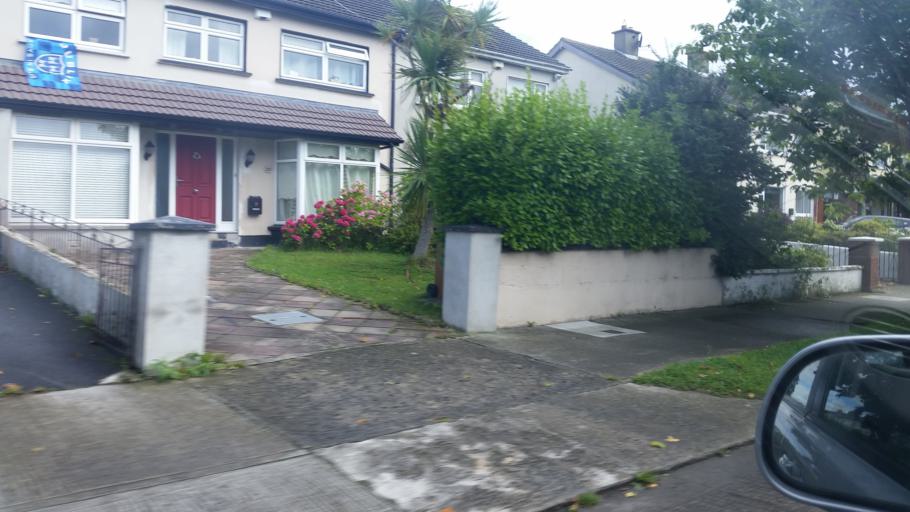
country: IE
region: Leinster
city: Portmarnock
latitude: 53.4339
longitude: -6.1330
